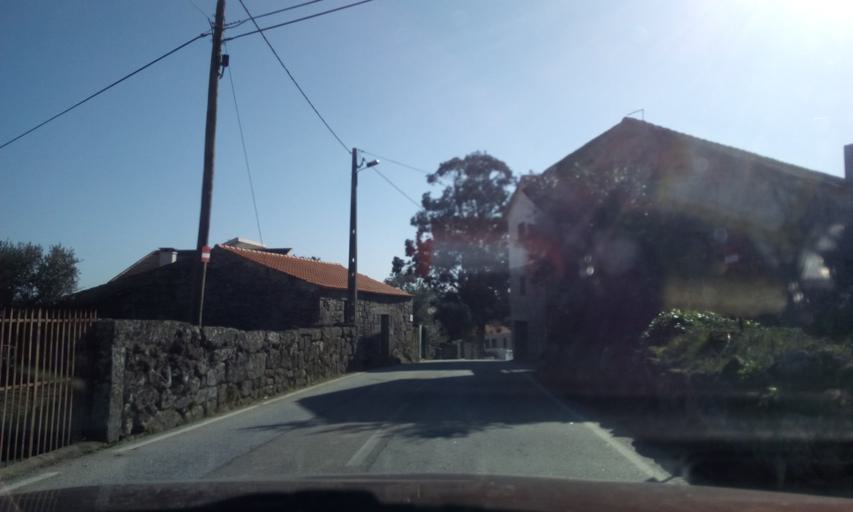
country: PT
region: Guarda
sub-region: Celorico da Beira
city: Celorico da Beira
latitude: 40.6728
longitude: -7.3969
